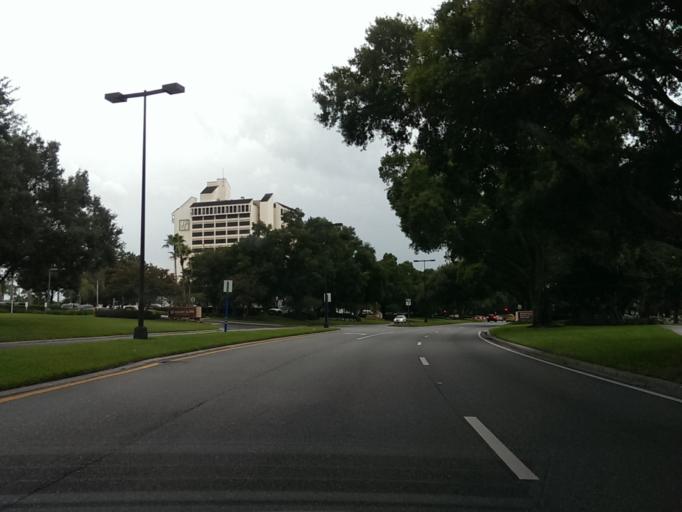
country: US
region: Florida
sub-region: Osceola County
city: Celebration
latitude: 28.3774
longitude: -81.5077
